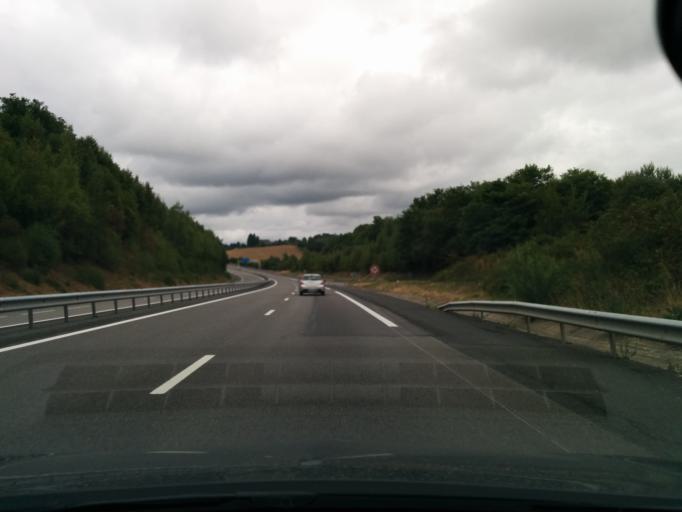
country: FR
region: Limousin
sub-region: Departement de la Correze
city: Saint-Mexant
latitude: 45.3088
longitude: 1.5757
